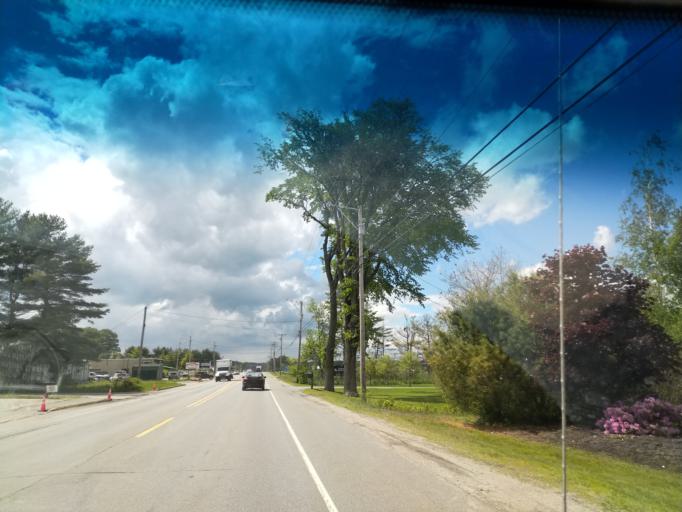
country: US
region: Maine
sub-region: Cumberland County
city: Westbrook
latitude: 43.6876
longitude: -70.3925
